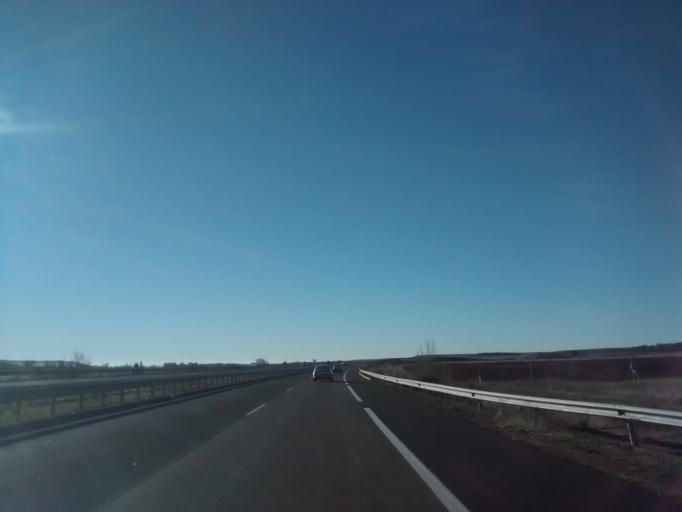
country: ES
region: Castille and Leon
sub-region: Provincia de Palencia
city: Villaprovedo
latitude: 42.5016
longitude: -4.3802
